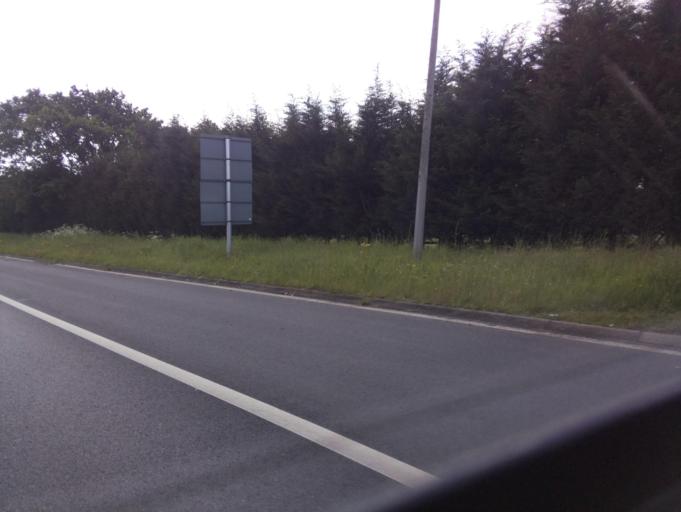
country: GB
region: England
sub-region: North Lincolnshire
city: Manton
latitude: 53.5620
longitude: -0.6005
